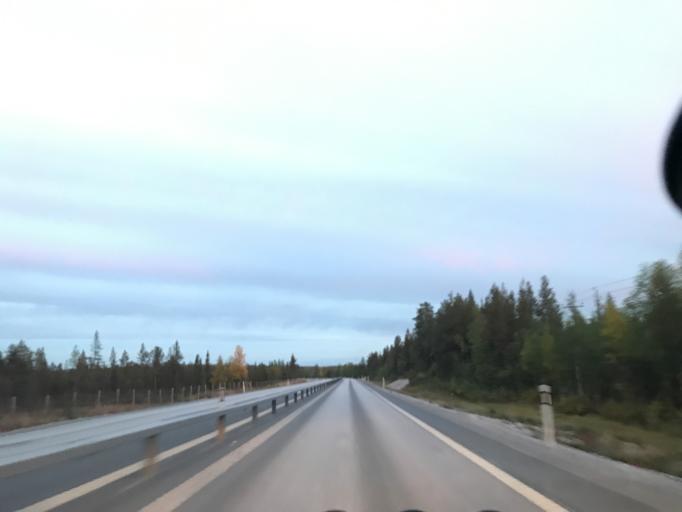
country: SE
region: Norrbotten
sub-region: Gallivare Kommun
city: Malmberget
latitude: 67.6633
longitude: 20.9928
